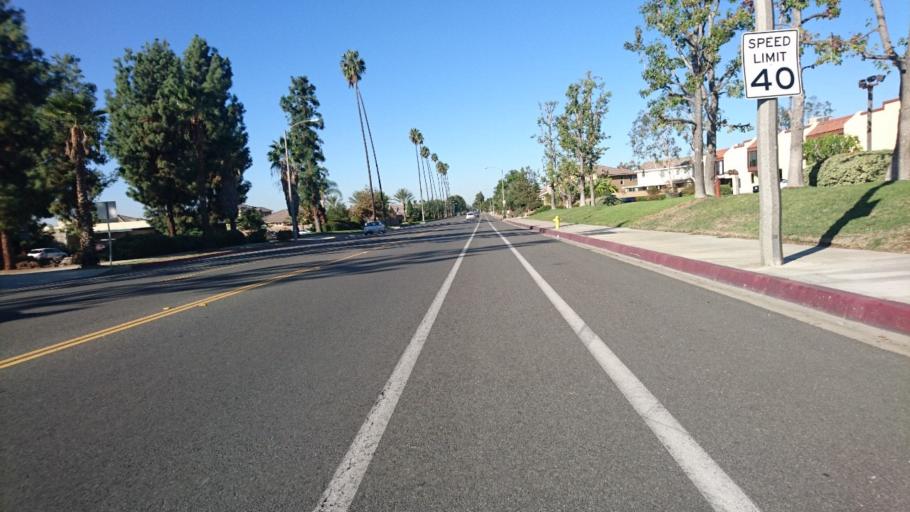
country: US
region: California
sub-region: Los Angeles County
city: Claremont
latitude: 34.0964
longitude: -117.7375
